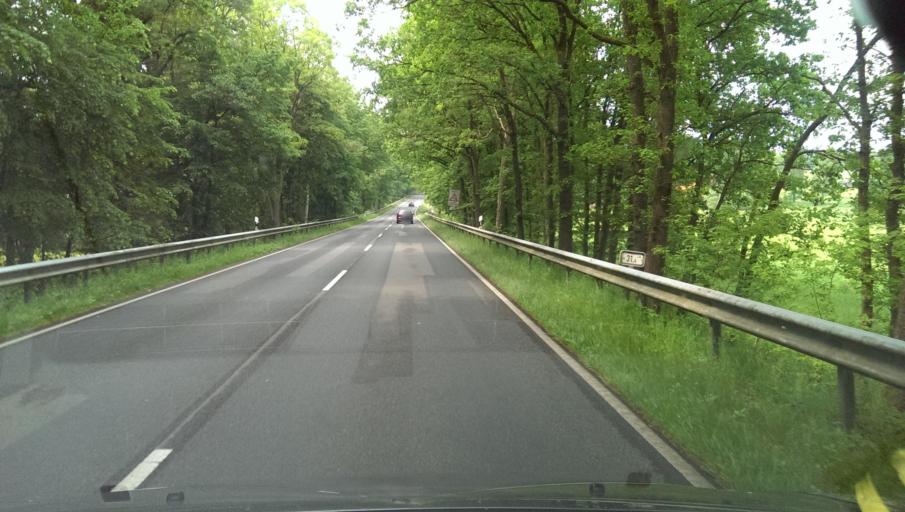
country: DE
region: Lower Saxony
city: Unterluss
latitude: 52.7961
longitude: 10.3824
